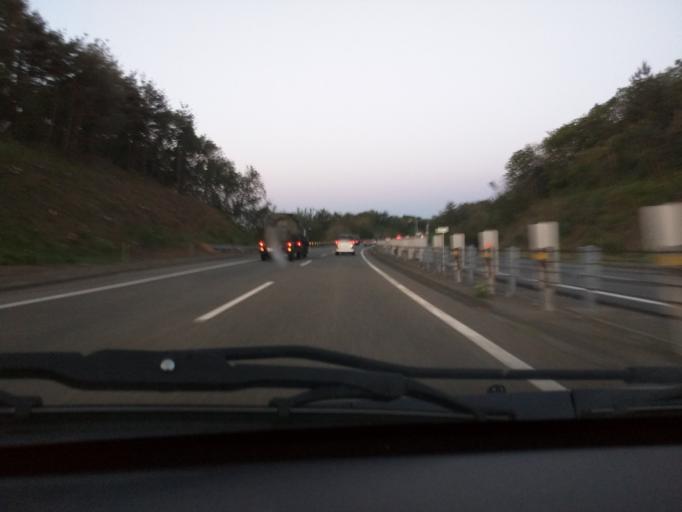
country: JP
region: Niigata
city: Kashiwazaki
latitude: 37.3487
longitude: 138.5024
